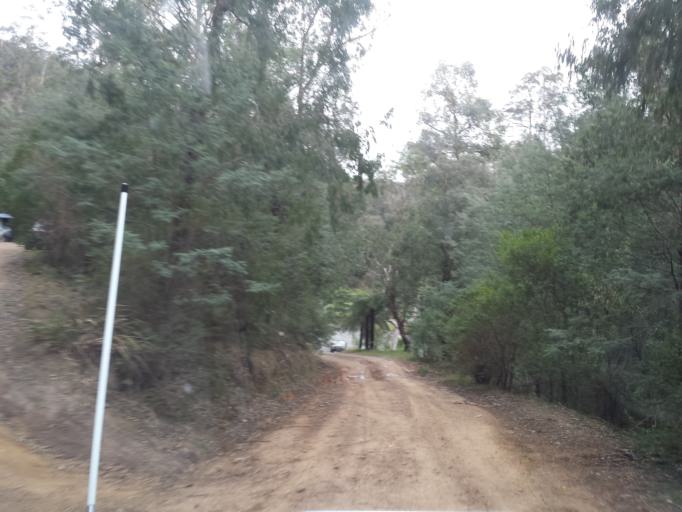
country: AU
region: Victoria
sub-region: Latrobe
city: Traralgon
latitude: -37.9973
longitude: 146.4733
